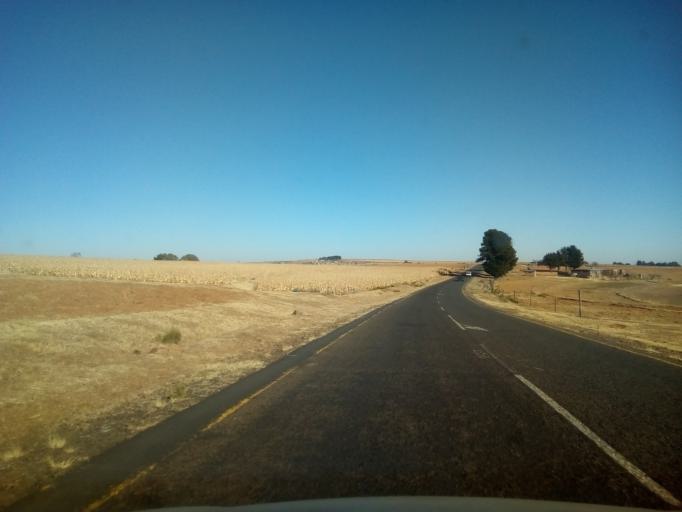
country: LS
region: Maseru
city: Maseru
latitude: -29.2930
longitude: 27.6323
